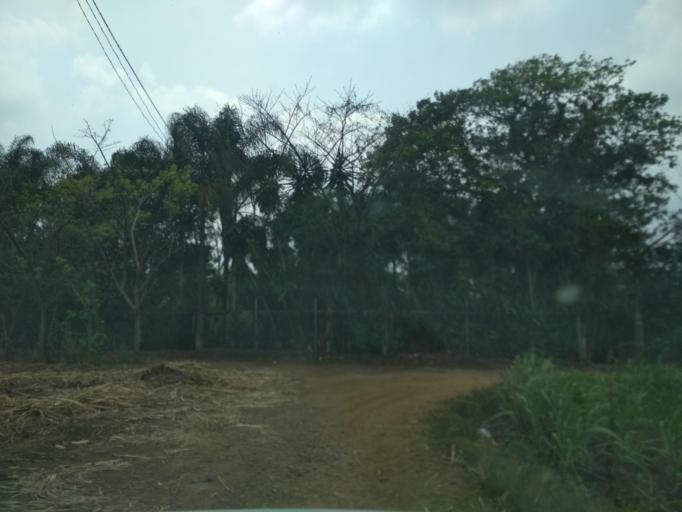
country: MX
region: Veracruz
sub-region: Cordoba
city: Fredepo
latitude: 18.8580
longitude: -96.9803
